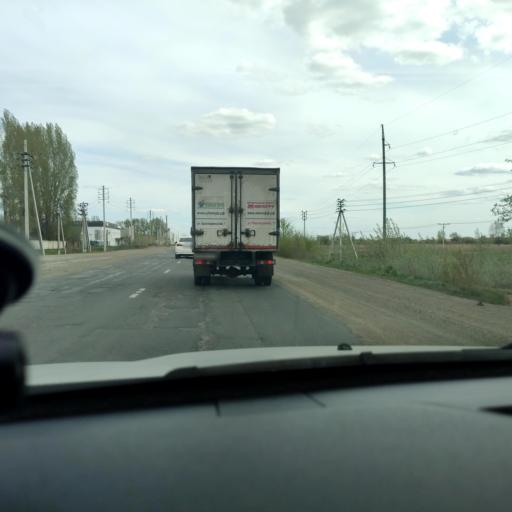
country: RU
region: Samara
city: Kinel'
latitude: 53.2348
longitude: 50.5854
